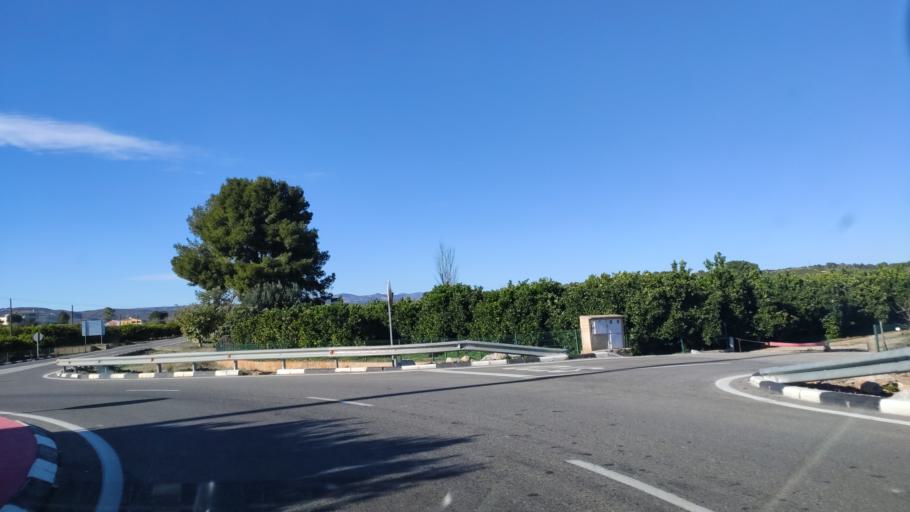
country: ES
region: Valencia
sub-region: Provincia de Valencia
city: Tous
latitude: 39.1275
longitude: -0.5563
